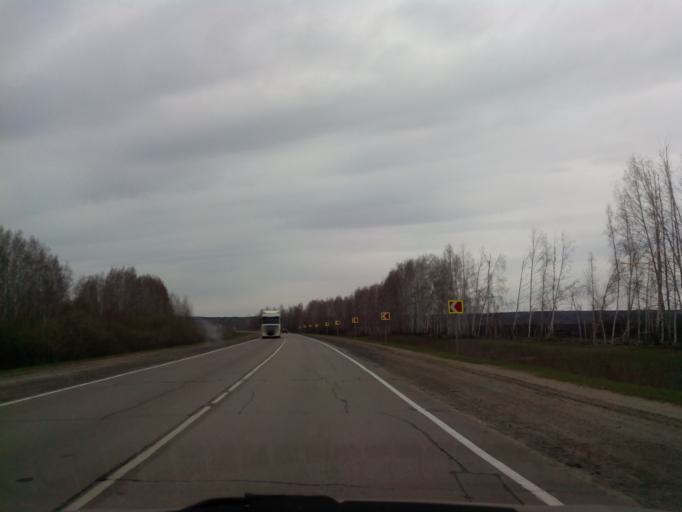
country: RU
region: Tambov
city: Znamenka
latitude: 52.5167
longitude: 41.3645
